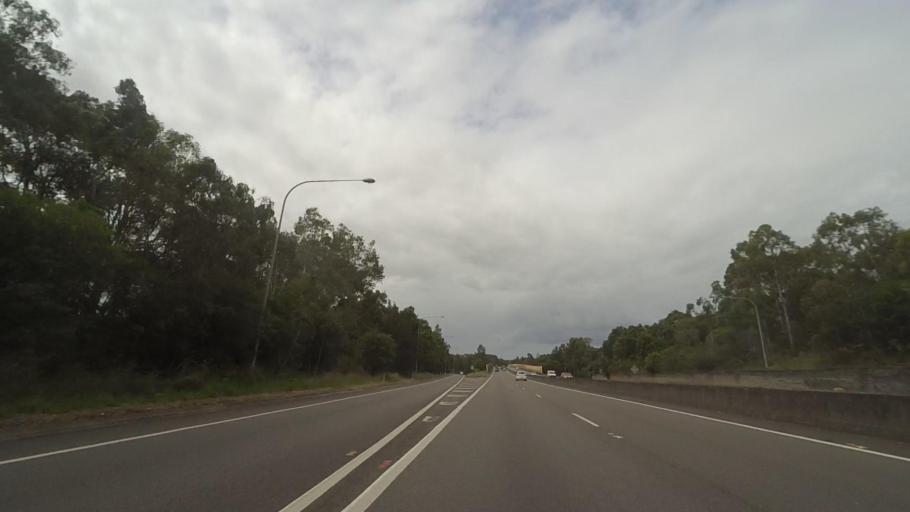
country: AU
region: New South Wales
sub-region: Port Stephens Shire
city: Raymond Terrace
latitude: -32.7592
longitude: 151.7646
